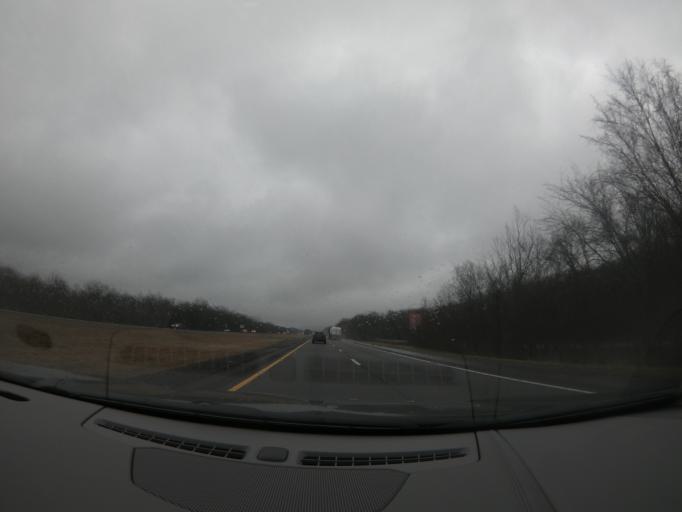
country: US
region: Tennessee
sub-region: Rutherford County
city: Plainview
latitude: 35.6764
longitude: -86.2852
